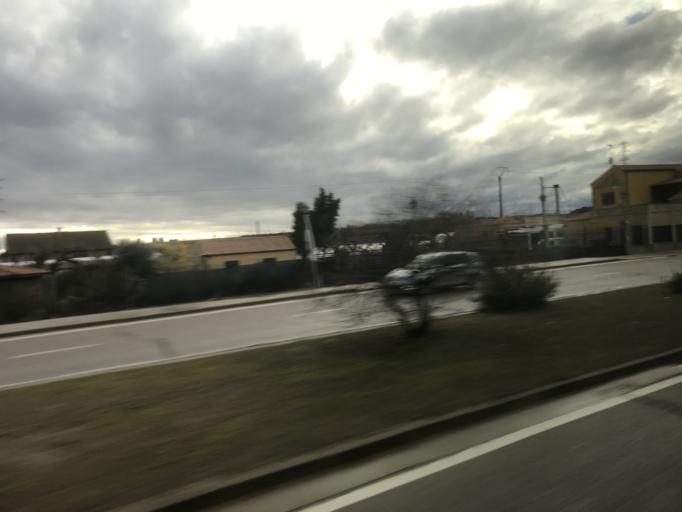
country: ES
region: Castille and Leon
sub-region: Provincia de Valladolid
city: Zaratan
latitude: 41.6514
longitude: -4.7616
